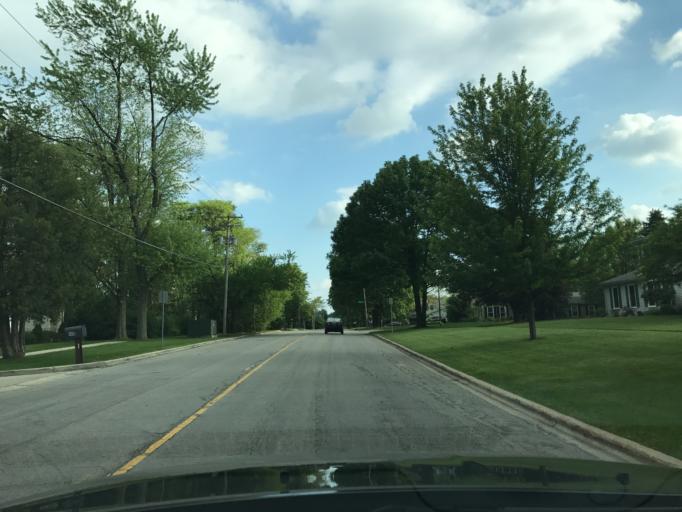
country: US
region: Illinois
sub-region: DuPage County
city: Naperville
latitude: 41.7687
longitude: -88.1204
